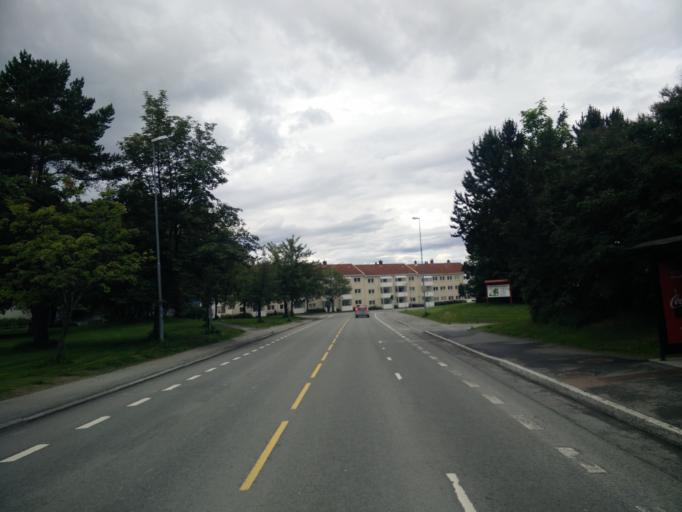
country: NO
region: Sor-Trondelag
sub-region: Trondheim
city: Trondheim
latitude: 63.4281
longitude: 10.4164
